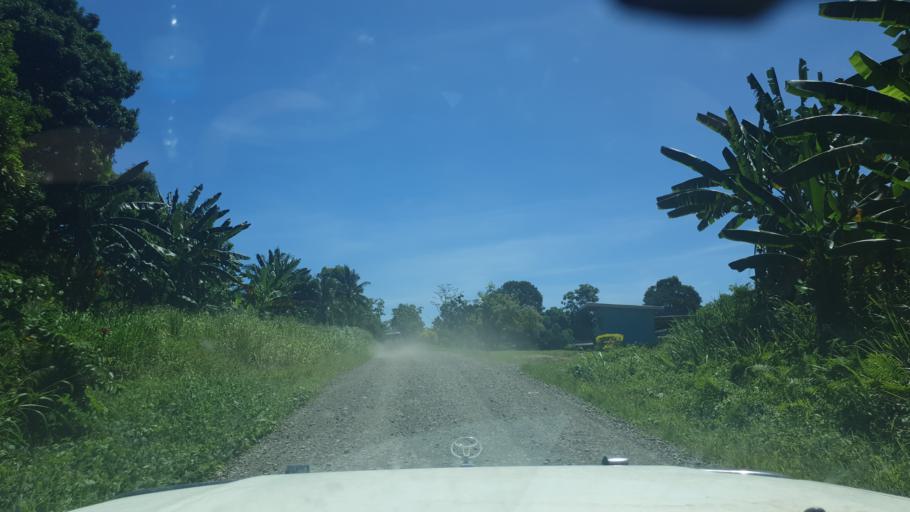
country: PG
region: Bougainville
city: Buka
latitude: -5.6640
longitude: 155.0986
